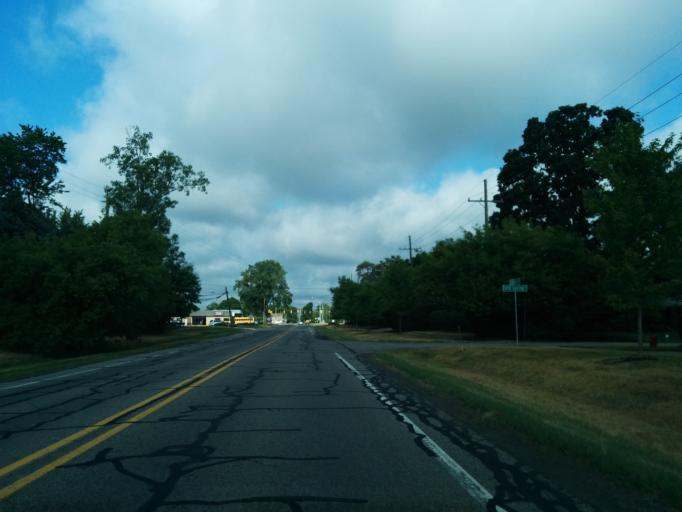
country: US
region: Michigan
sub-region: Oakland County
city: Franklin
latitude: 42.5291
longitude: -83.3367
